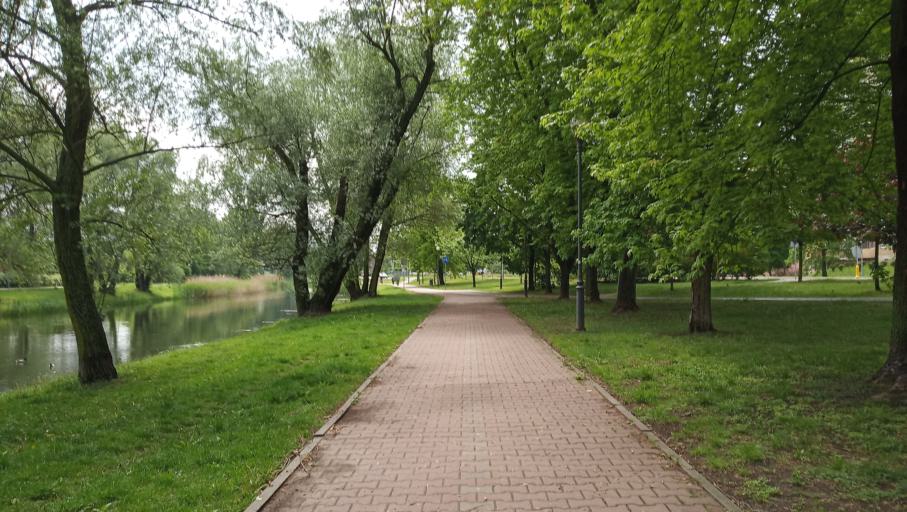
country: PL
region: Masovian Voivodeship
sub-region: Warszawa
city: Zoliborz
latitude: 52.2857
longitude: 20.9791
